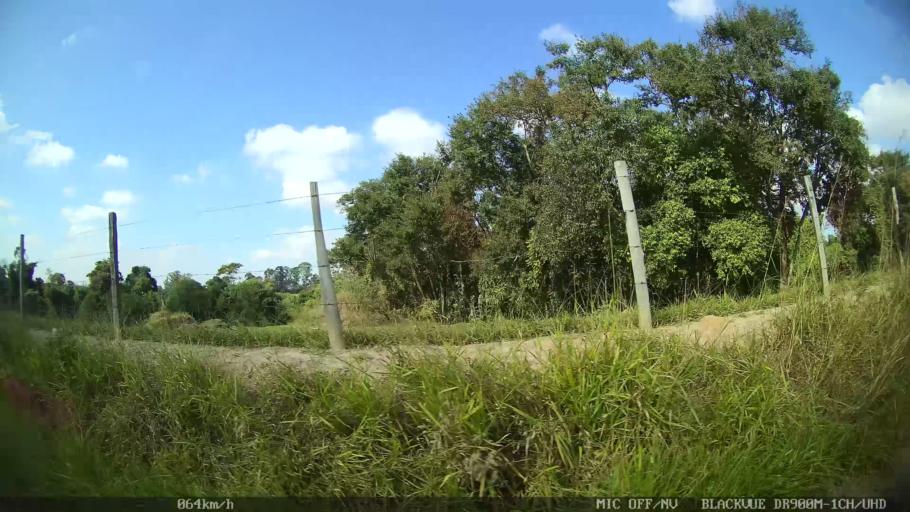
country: BR
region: Sao Paulo
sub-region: Indaiatuba
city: Indaiatuba
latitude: -22.9951
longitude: -47.1956
